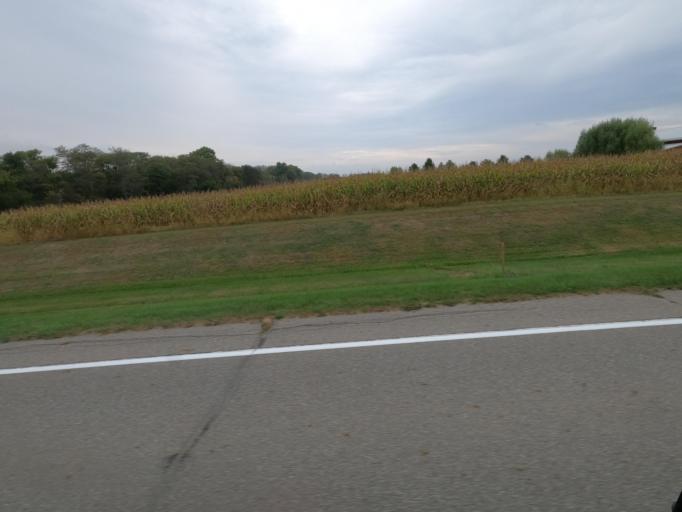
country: US
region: Iowa
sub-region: Van Buren County
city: Keosauqua
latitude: 40.8133
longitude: -91.7918
